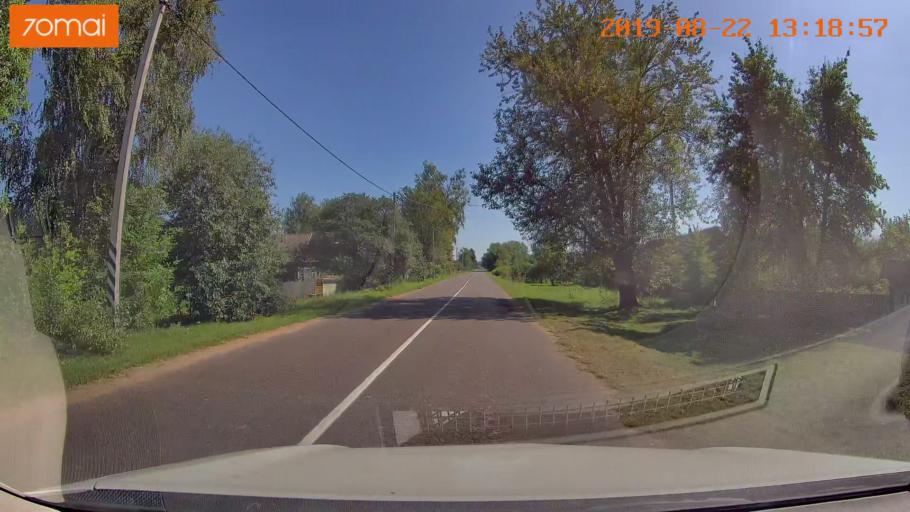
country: BY
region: Minsk
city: Urechcha
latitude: 53.2374
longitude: 27.9447
